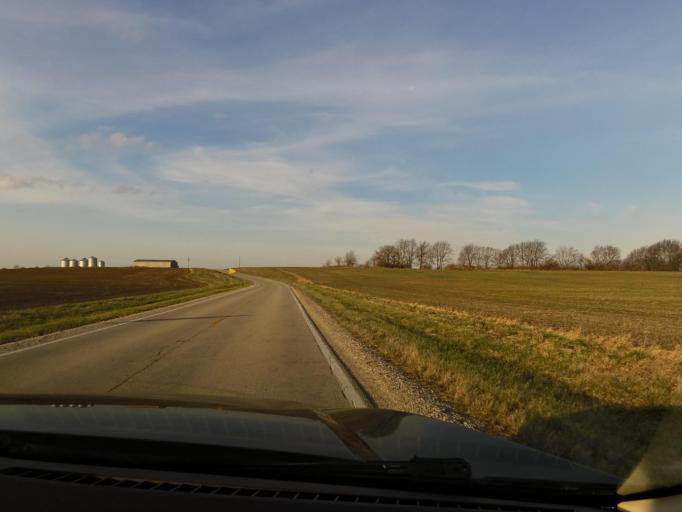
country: US
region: Illinois
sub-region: Fayette County
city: Vandalia
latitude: 38.9499
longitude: -89.1427
